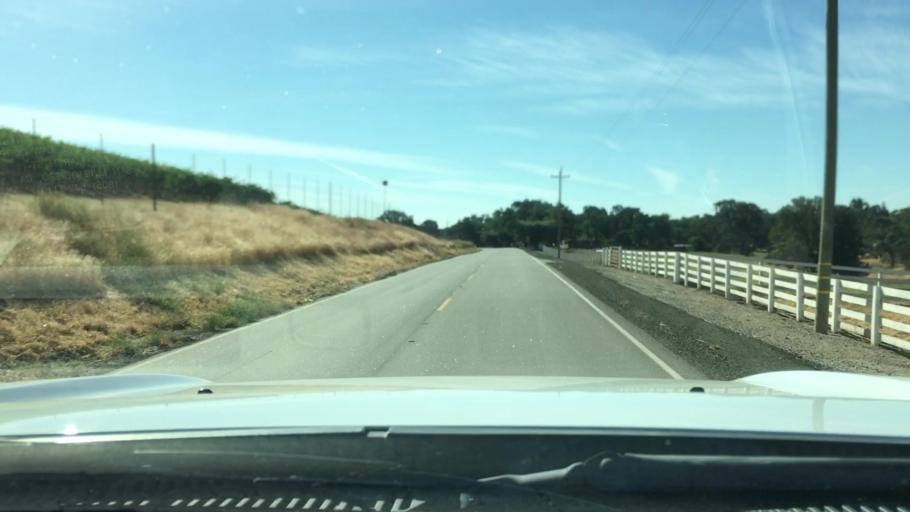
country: US
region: California
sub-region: San Luis Obispo County
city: Templeton
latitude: 35.5572
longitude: -120.6285
